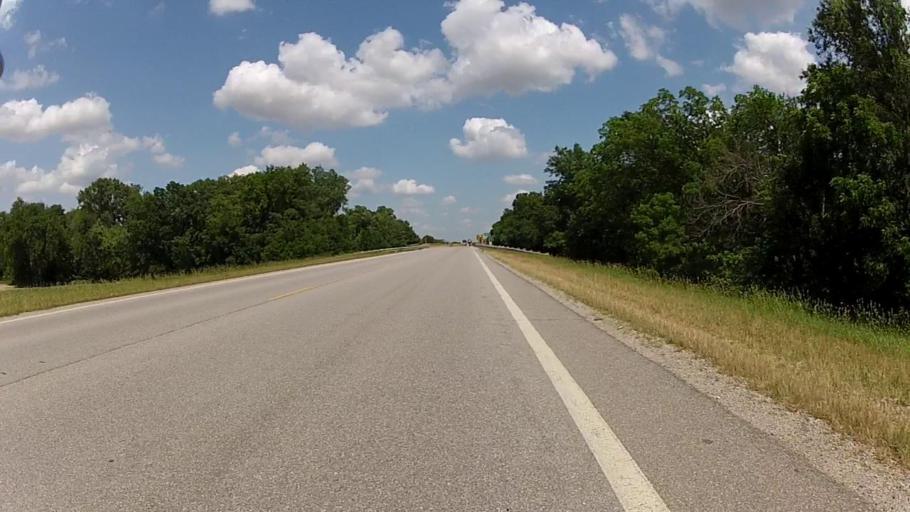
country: US
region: Kansas
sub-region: Labette County
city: Oswego
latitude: 37.1938
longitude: -95.1938
